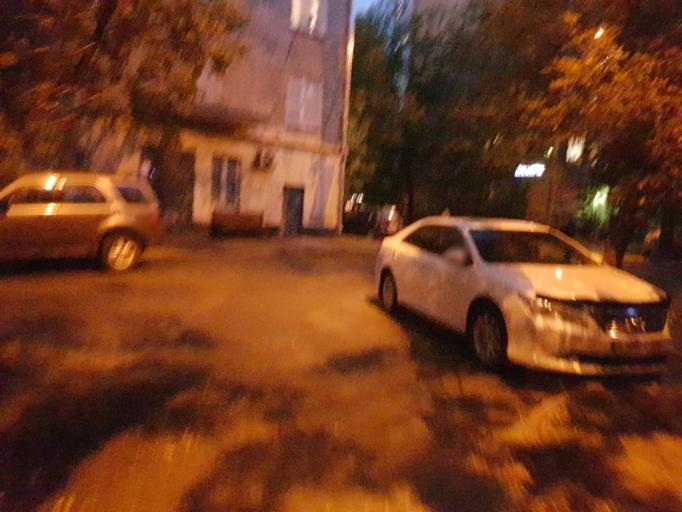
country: RU
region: Moskovskaya
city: Dorogomilovo
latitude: 55.7864
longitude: 37.5598
